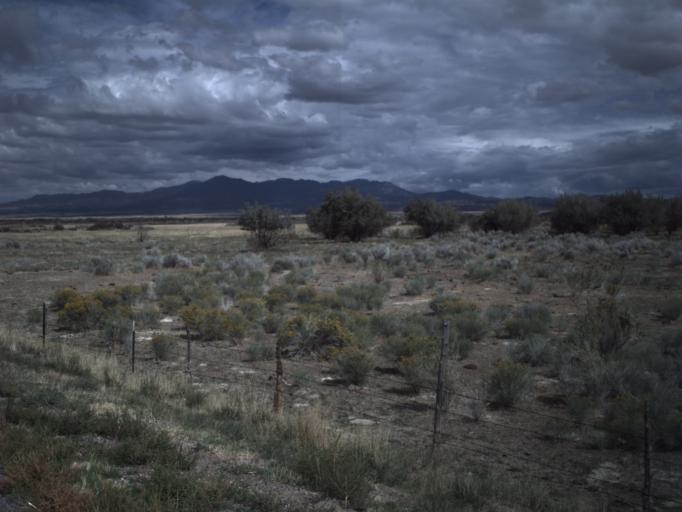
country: US
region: Utah
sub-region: Millard County
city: Fillmore
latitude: 39.1022
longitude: -112.4100
